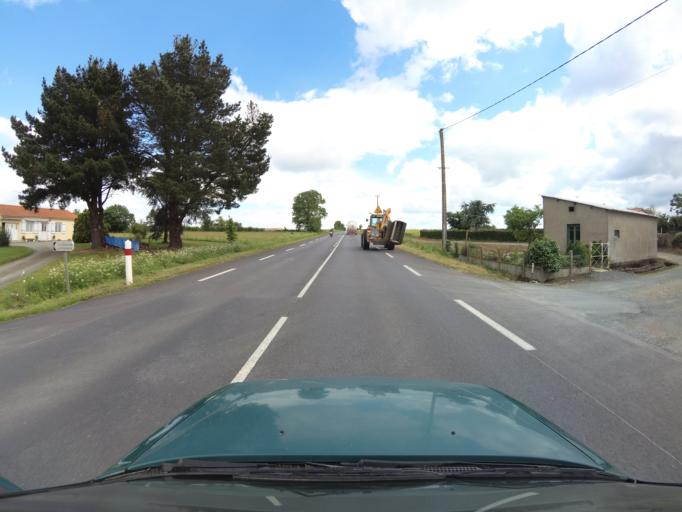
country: FR
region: Pays de la Loire
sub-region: Departement de la Vendee
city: Vendrennes
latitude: 46.8261
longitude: -1.1540
